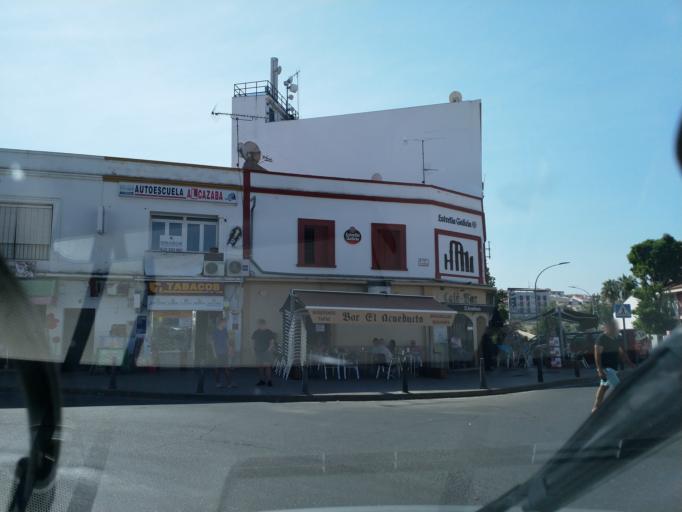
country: ES
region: Extremadura
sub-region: Provincia de Badajoz
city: Merida
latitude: 38.9253
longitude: -6.3486
